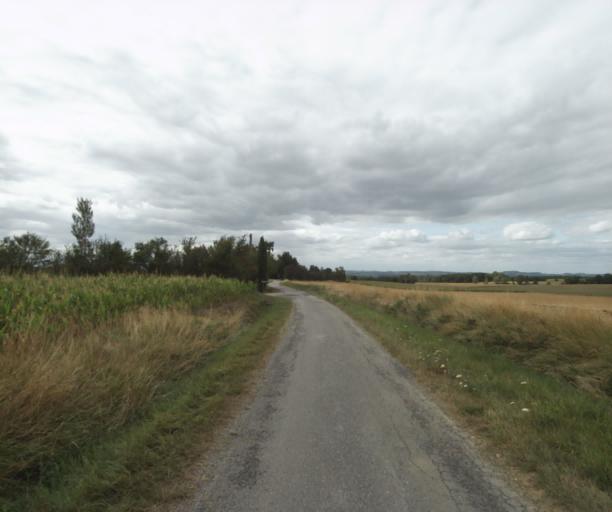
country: FR
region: Midi-Pyrenees
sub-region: Departement du Tarn
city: Soreze
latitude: 43.4600
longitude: 2.0680
